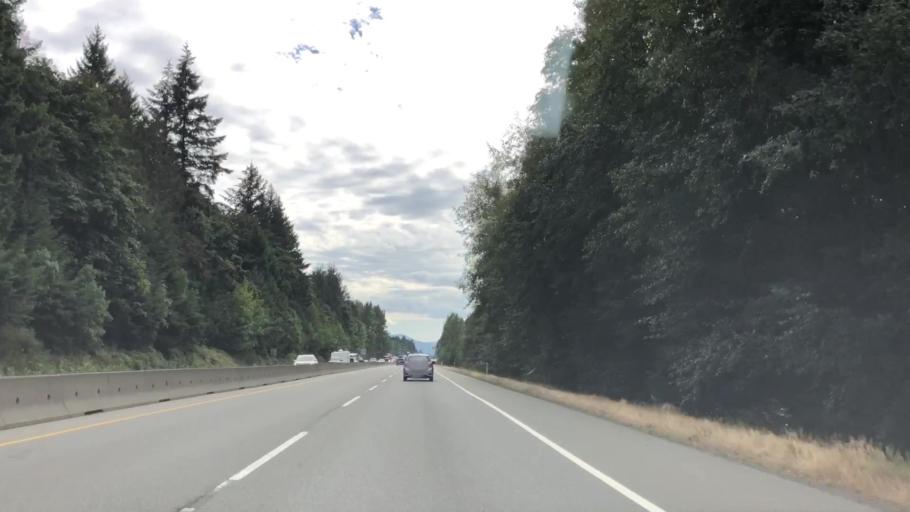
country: CA
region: British Columbia
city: North Cowichan
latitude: 48.8420
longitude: -123.7181
